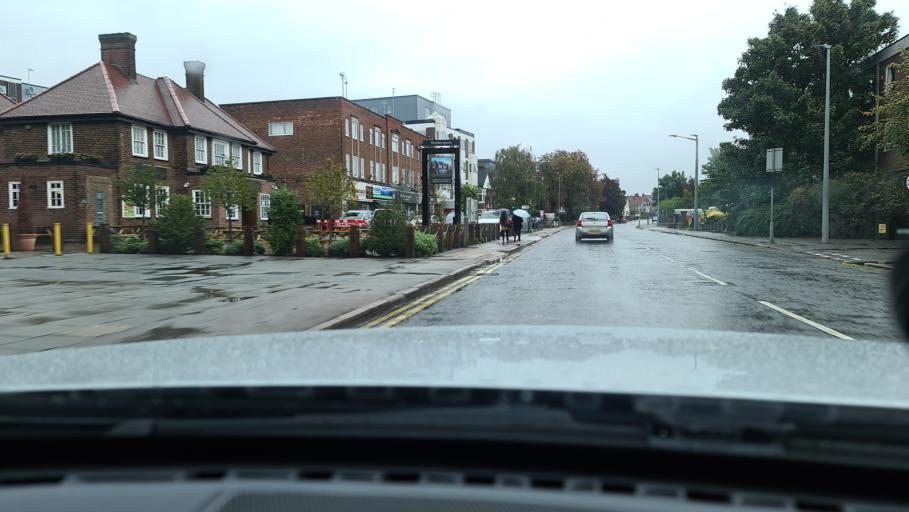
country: GB
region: England
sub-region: Buckinghamshire
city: Bletchley
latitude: 51.9954
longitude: -0.7267
